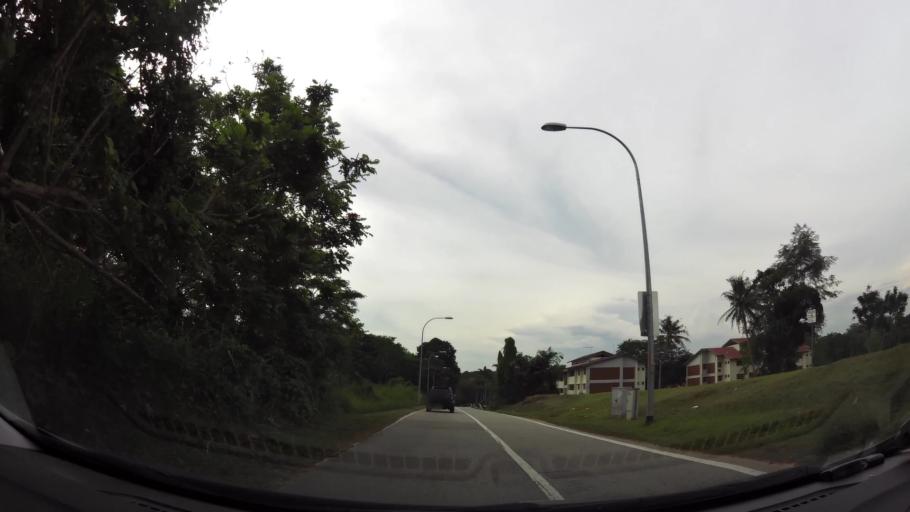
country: MY
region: Johor
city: Johor Bahru
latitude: 1.4206
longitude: 103.7050
